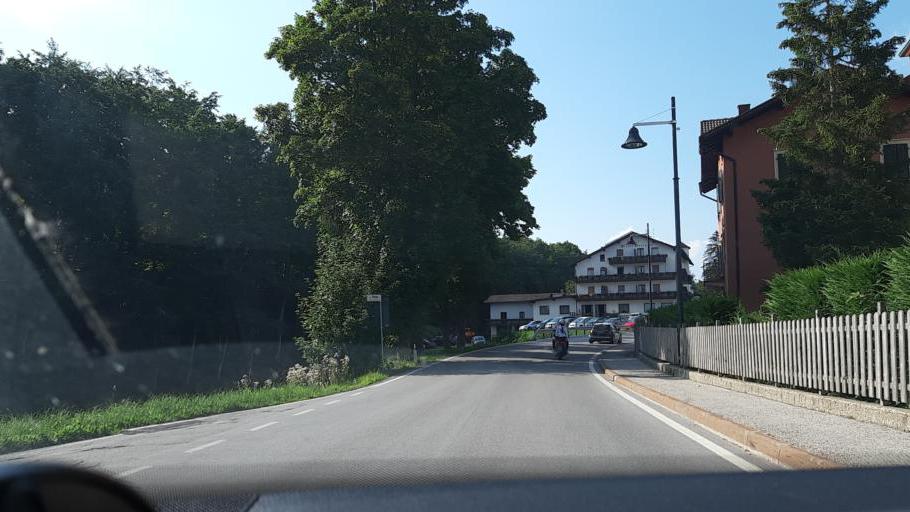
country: IT
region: Trentino-Alto Adige
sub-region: Provincia di Trento
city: Gionghi-Cappella
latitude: 45.9427
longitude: 11.2492
